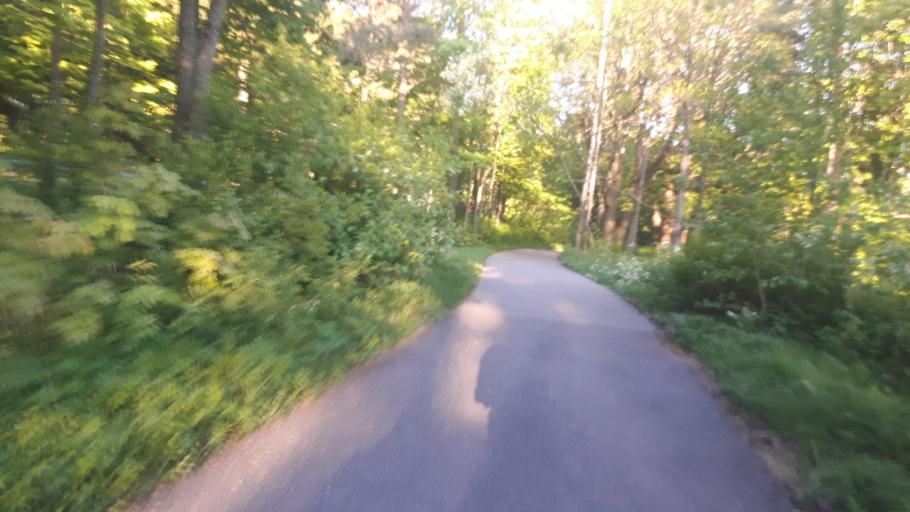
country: RU
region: Leningrad
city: Roshchino
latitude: 60.1949
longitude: 29.6225
